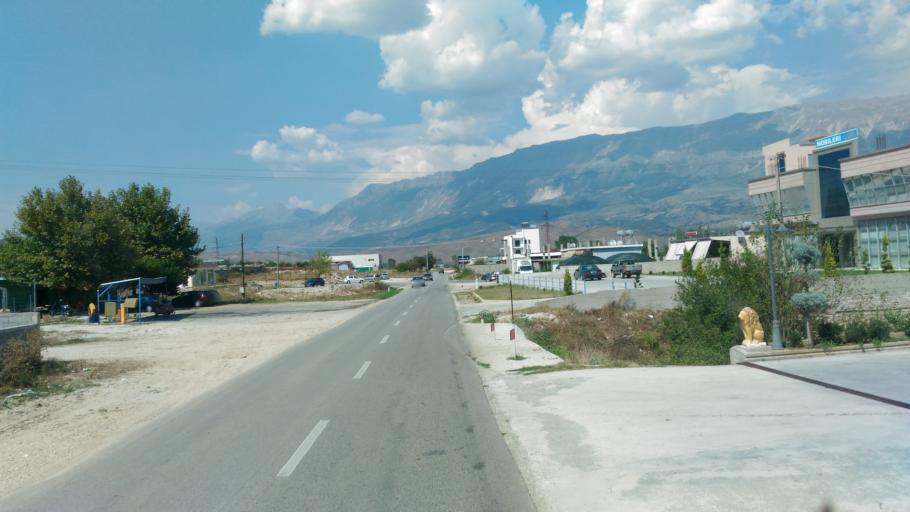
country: AL
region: Gjirokaster
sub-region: Rrethi i Gjirokastres
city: Dervician
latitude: 40.0479
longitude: 20.1769
